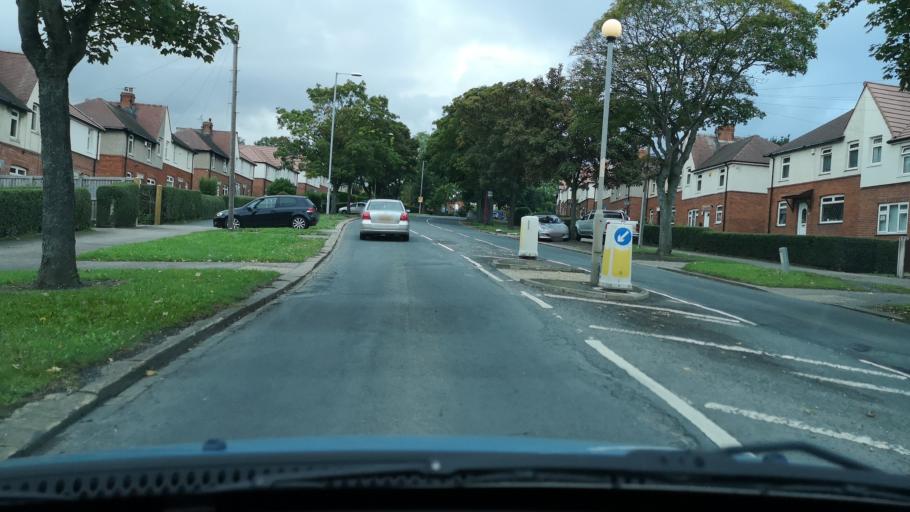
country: GB
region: England
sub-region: City and Borough of Wakefield
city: Crigglestone
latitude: 53.6698
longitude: -1.5338
